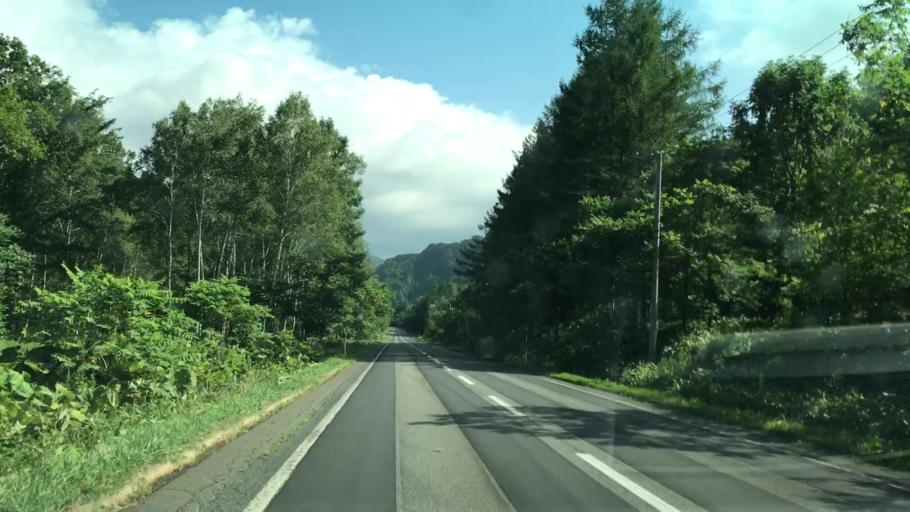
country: JP
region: Hokkaido
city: Shizunai-furukawacho
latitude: 42.8320
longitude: 142.4159
